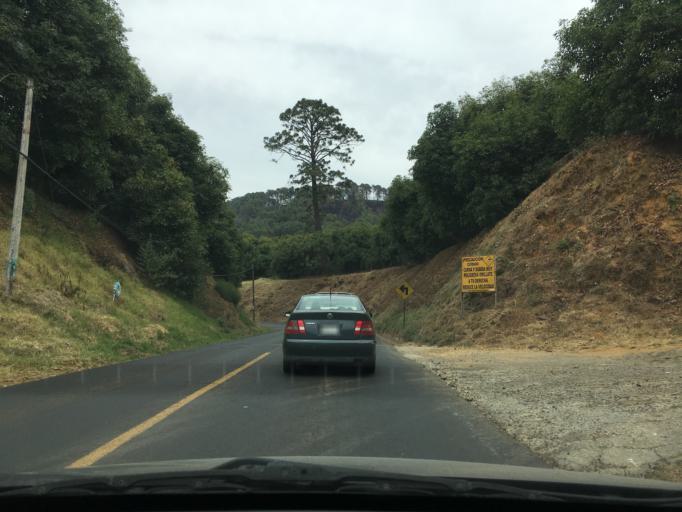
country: MX
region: Michoacan
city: Nuevo San Juan Parangaricutiro
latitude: 19.4034
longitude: -102.1088
